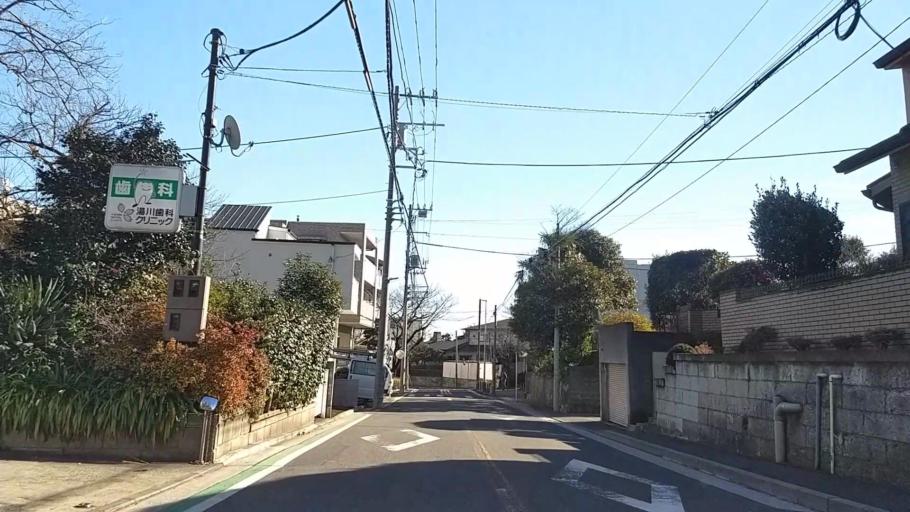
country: JP
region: Kanagawa
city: Yokohama
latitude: 35.4509
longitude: 139.5856
